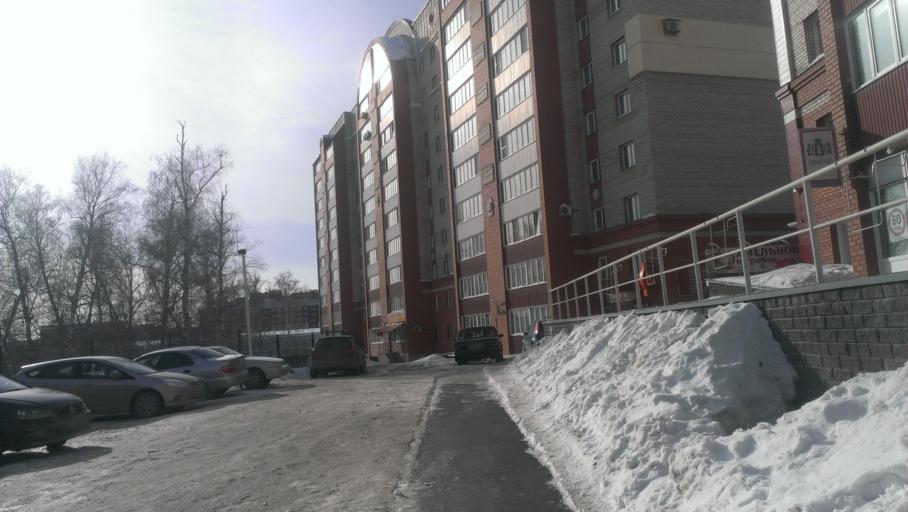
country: RU
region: Altai Krai
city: Novosilikatnyy
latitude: 53.3617
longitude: 83.6664
